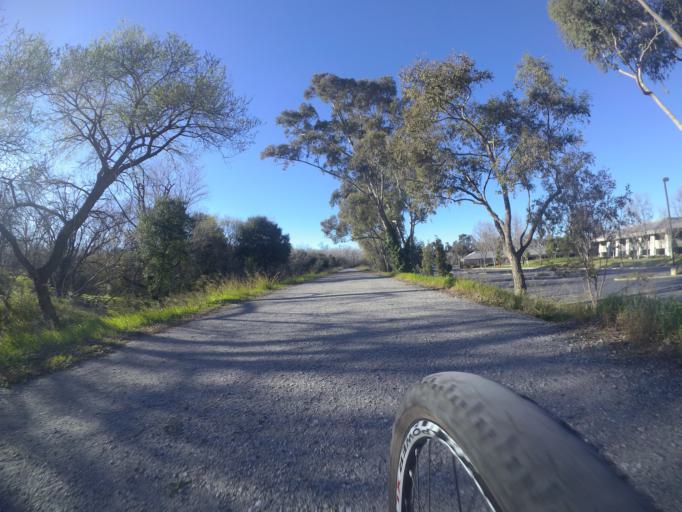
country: US
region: California
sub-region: Santa Clara County
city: Milpitas
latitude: 37.4063
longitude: -121.9212
